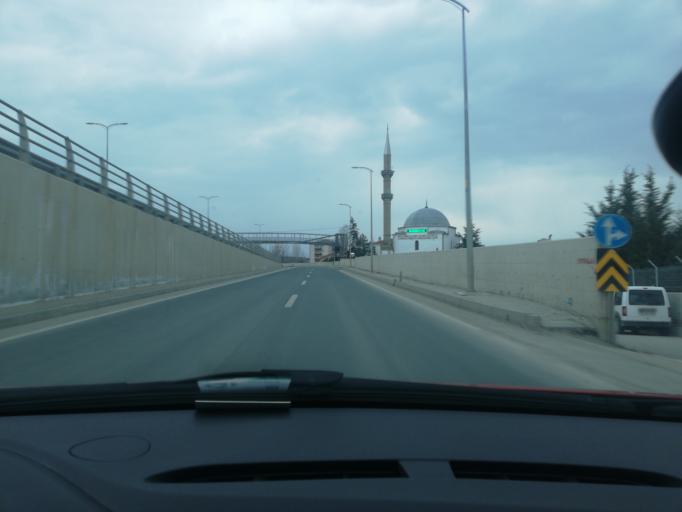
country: TR
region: Kastamonu
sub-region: Cide
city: Kastamonu
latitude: 41.4177
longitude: 33.7997
